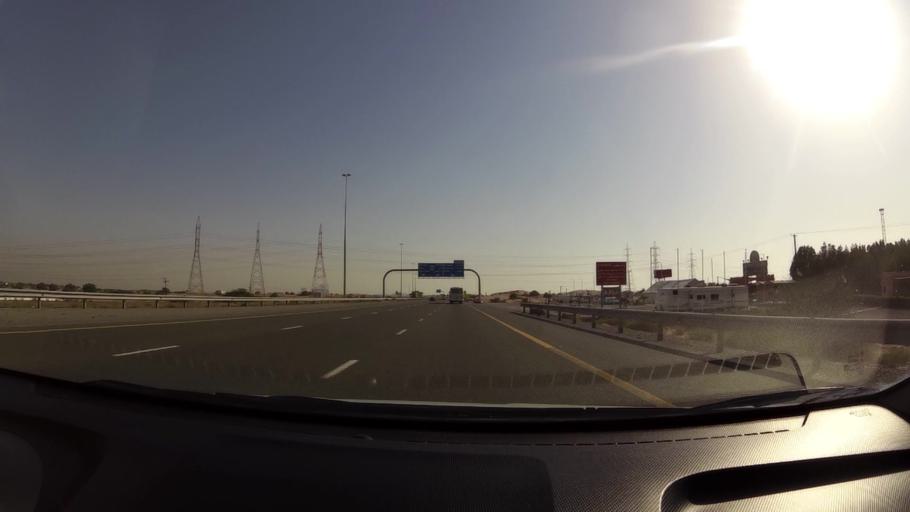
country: AE
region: Umm al Qaywayn
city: Umm al Qaywayn
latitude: 25.4428
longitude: 55.6052
